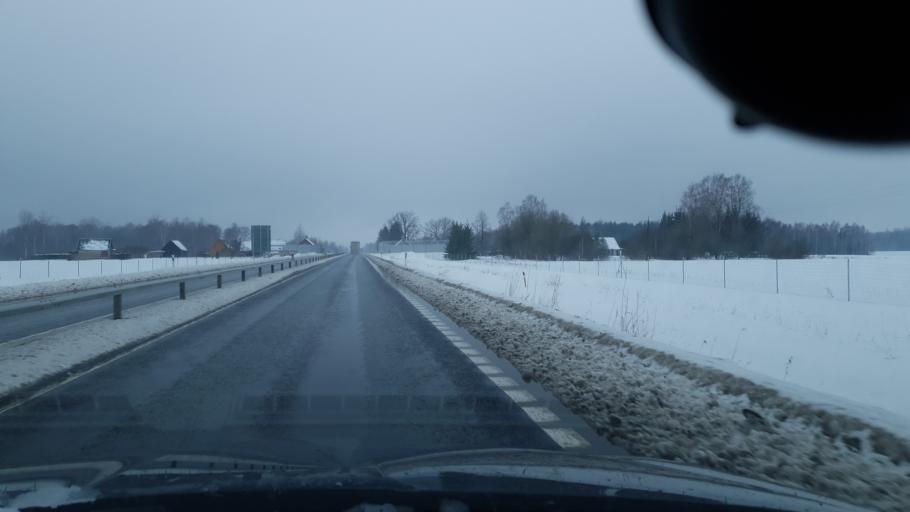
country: EE
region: Tartu
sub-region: Puhja vald
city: Puhja
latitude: 58.4460
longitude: 26.4373
